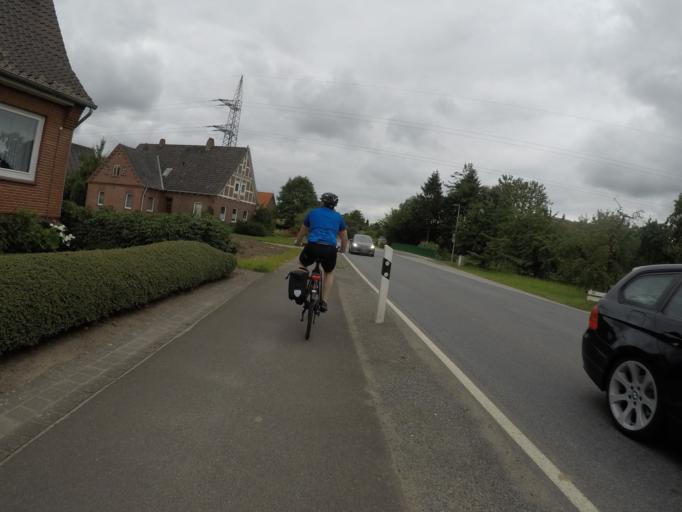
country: DE
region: Schleswig-Holstein
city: Haseldorf
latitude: 53.5914
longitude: 9.5638
